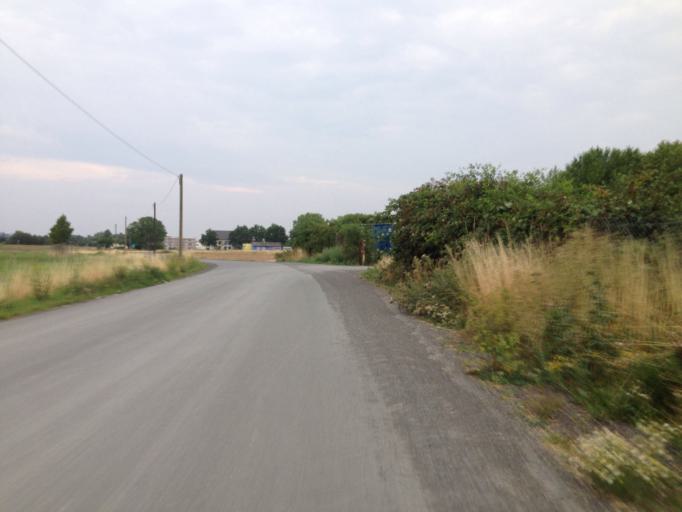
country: DE
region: Hesse
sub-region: Regierungsbezirk Giessen
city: Giessen
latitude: 50.6034
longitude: 8.6611
